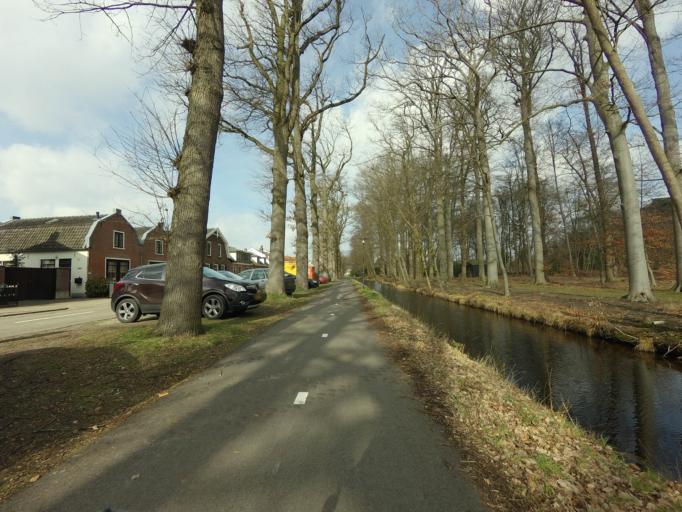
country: NL
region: North Holland
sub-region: Gemeente Wijdemeren
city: Kortenhoef
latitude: 52.2341
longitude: 5.1220
